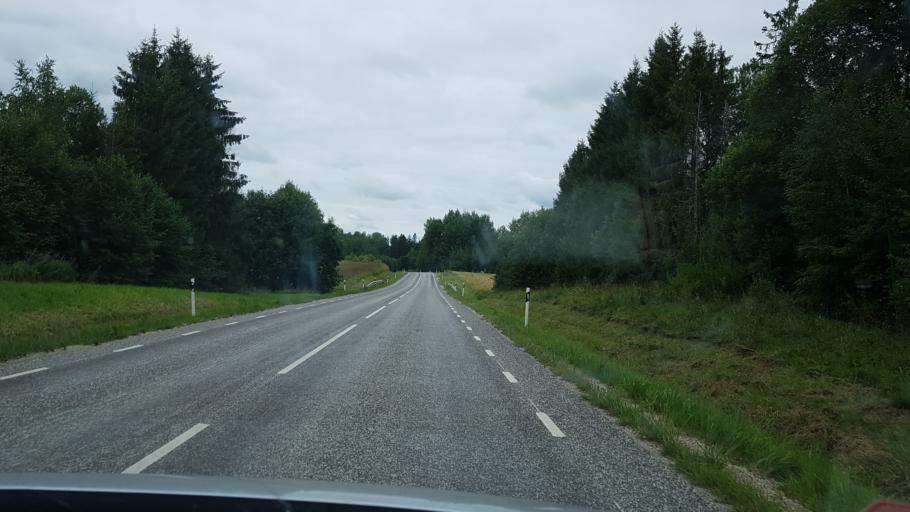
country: EE
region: Vorumaa
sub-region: Antsla vald
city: Vana-Antsla
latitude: 58.0044
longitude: 26.6381
